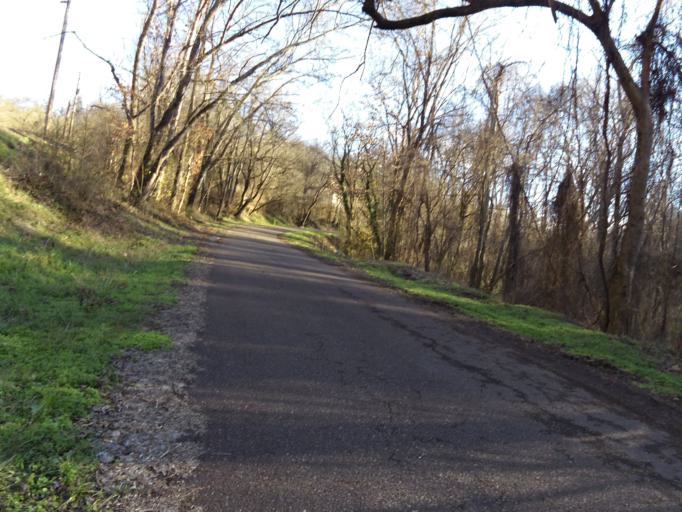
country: US
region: Tennessee
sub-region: Knox County
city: Knoxville
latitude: 35.9498
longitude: -83.8769
